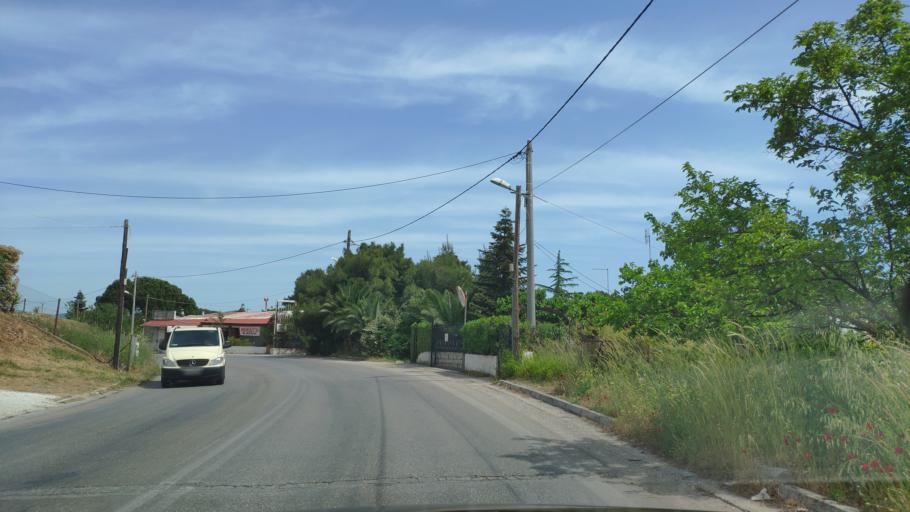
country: GR
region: Attica
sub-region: Nomarchia Anatolikis Attikis
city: Agios Stefanos
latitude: 38.1538
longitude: 23.8578
